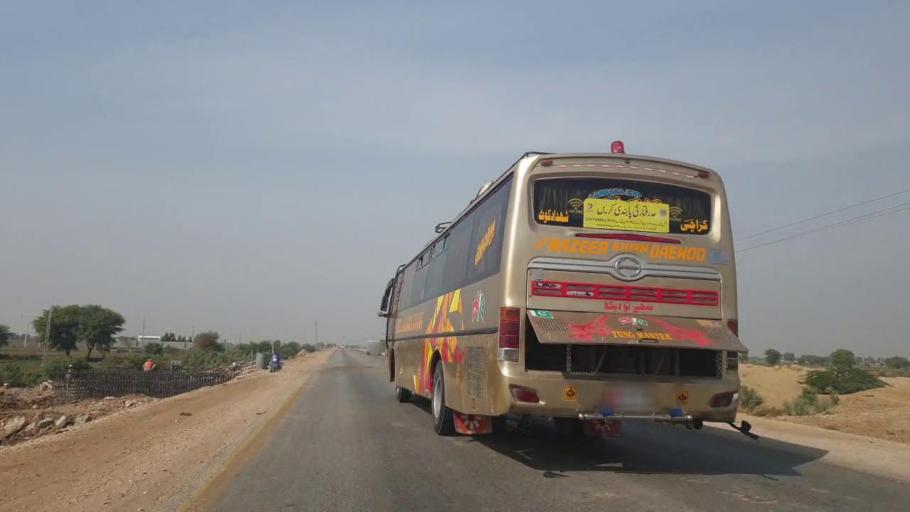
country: PK
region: Sindh
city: Sann
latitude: 26.0750
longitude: 68.0971
